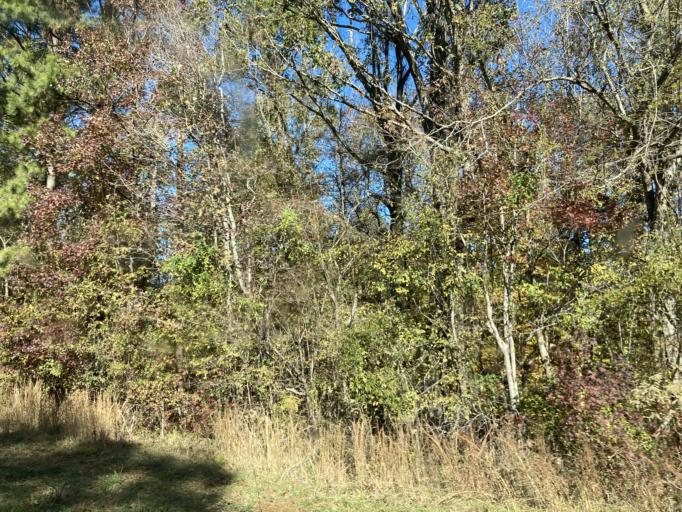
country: US
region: Mississippi
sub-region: Hinds County
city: Lynchburg
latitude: 32.5717
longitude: -90.5455
